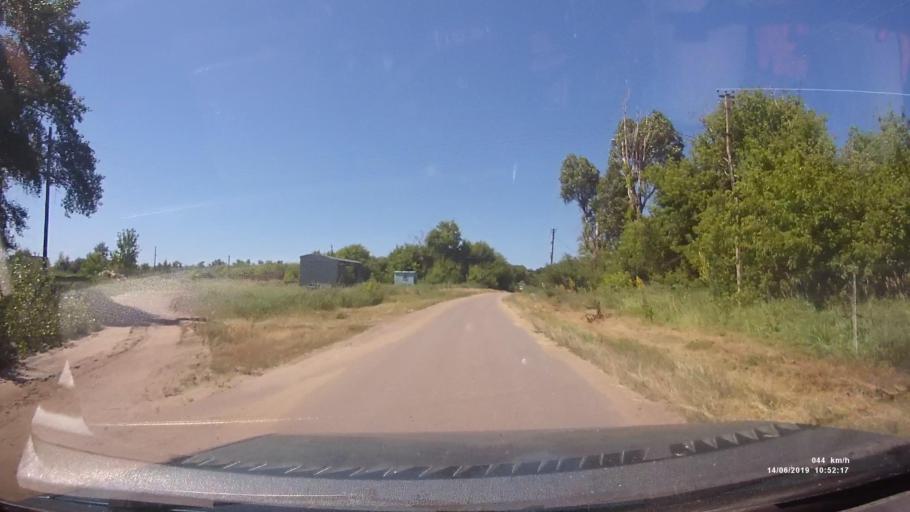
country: RU
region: Rostov
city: Kazanskaya
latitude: 49.8661
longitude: 41.3884
